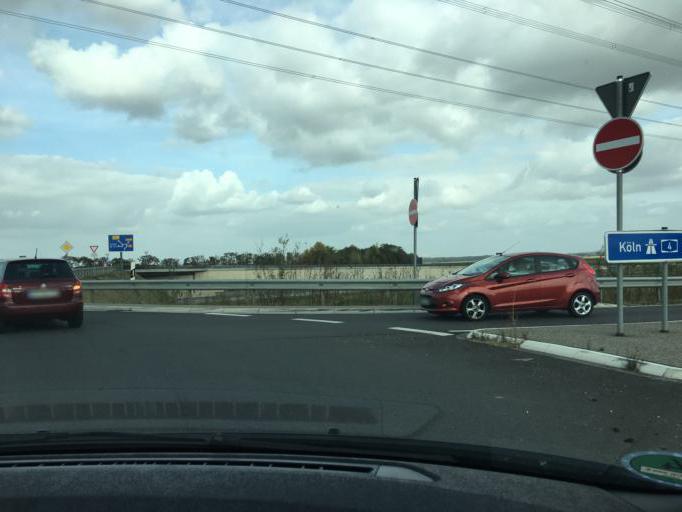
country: DE
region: North Rhine-Westphalia
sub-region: Regierungsbezirk Koln
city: Inden
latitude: 50.8342
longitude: 6.3835
